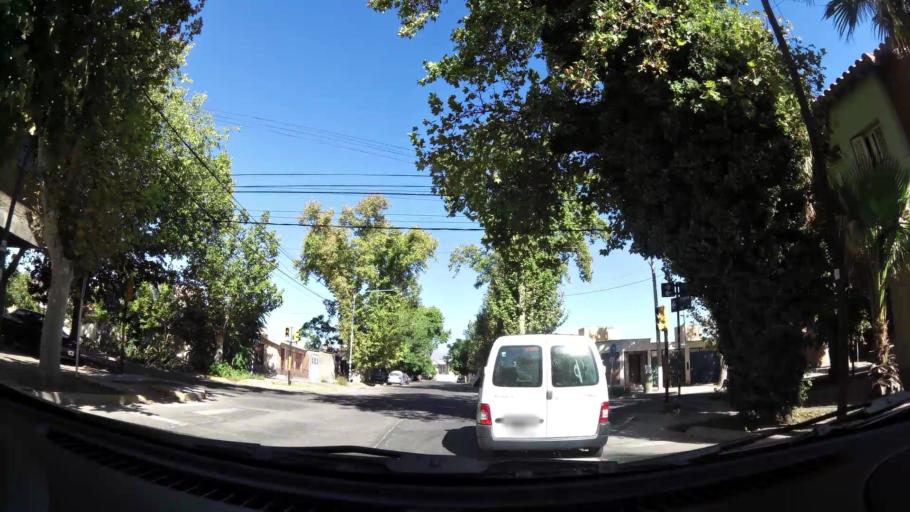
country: AR
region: Mendoza
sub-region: Departamento de Godoy Cruz
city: Godoy Cruz
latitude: -32.9249
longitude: -68.8624
